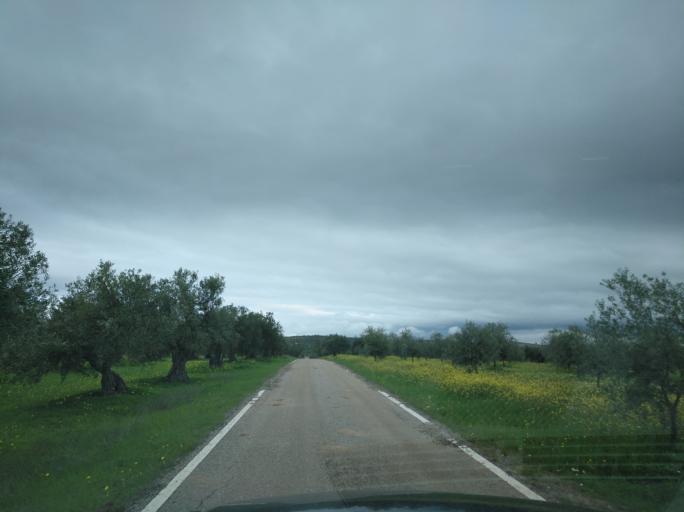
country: PT
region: Portalegre
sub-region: Campo Maior
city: Campo Maior
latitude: 38.9770
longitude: -7.0287
